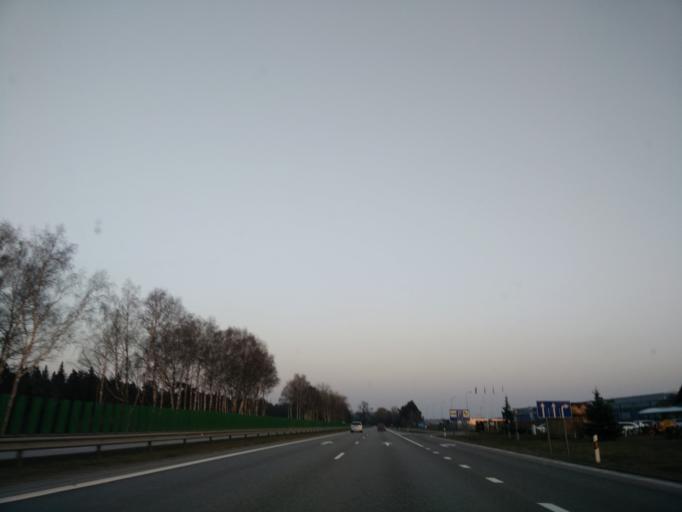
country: LT
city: Lentvaris
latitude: 54.7030
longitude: 25.0058
